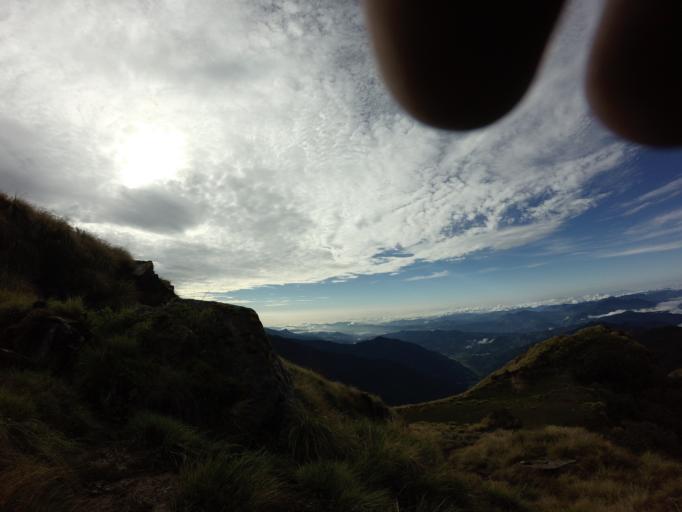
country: NP
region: Western Region
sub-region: Dhawalagiri Zone
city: Chitre
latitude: 28.4391
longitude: 83.8726
